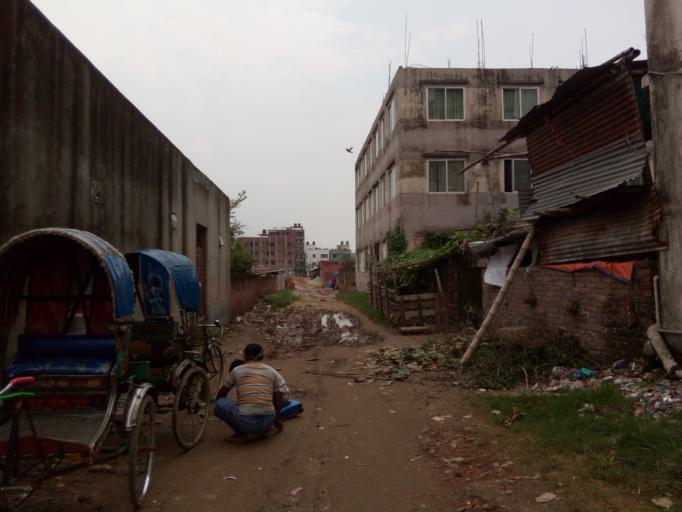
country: BD
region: Dhaka
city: Azimpur
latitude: 23.7564
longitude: 90.3525
